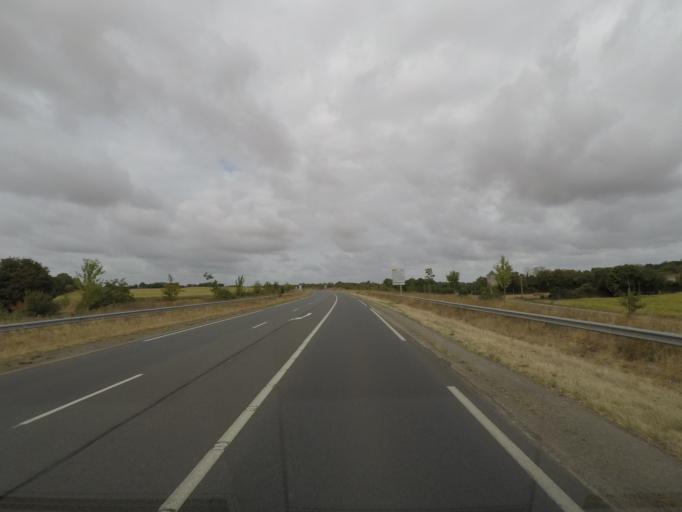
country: FR
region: Poitou-Charentes
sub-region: Departement des Deux-Sevres
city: Thorigne
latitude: 46.2860
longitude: -0.2685
